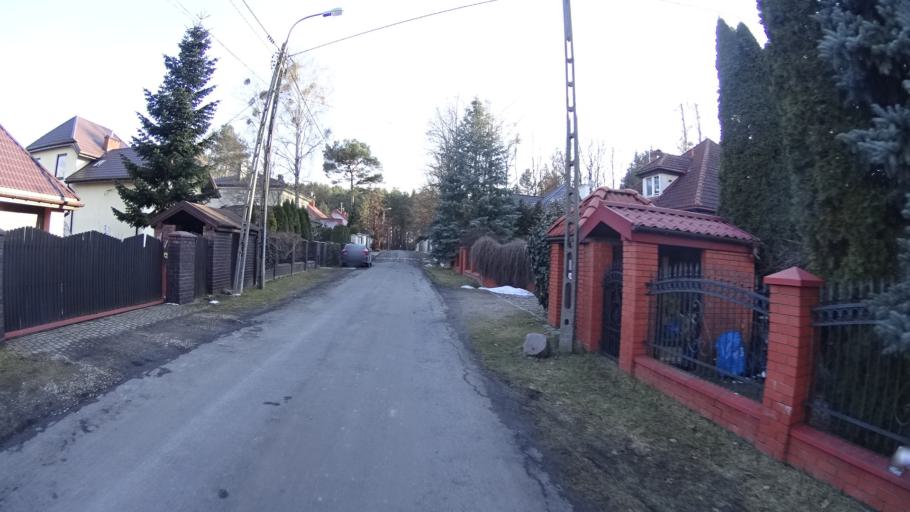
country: PL
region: Masovian Voivodeship
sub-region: Powiat warszawski zachodni
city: Hornowek
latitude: 52.2636
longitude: 20.7874
